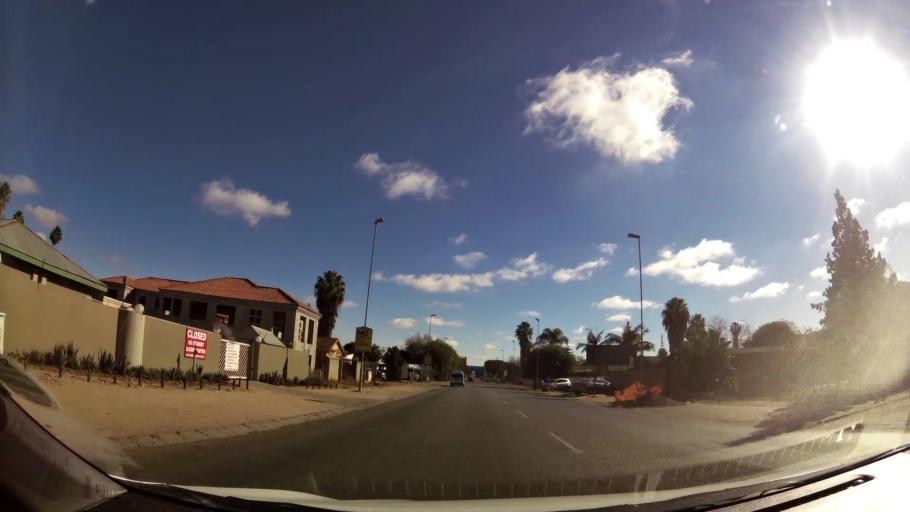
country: ZA
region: Limpopo
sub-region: Capricorn District Municipality
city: Polokwane
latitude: -23.9199
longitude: 29.4521
